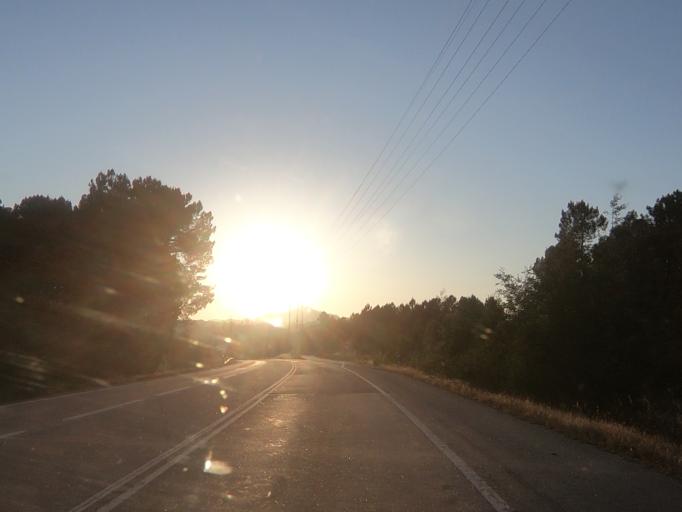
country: PT
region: Viseu
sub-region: Viseu
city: Rio de Loba
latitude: 40.6784
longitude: -7.8745
